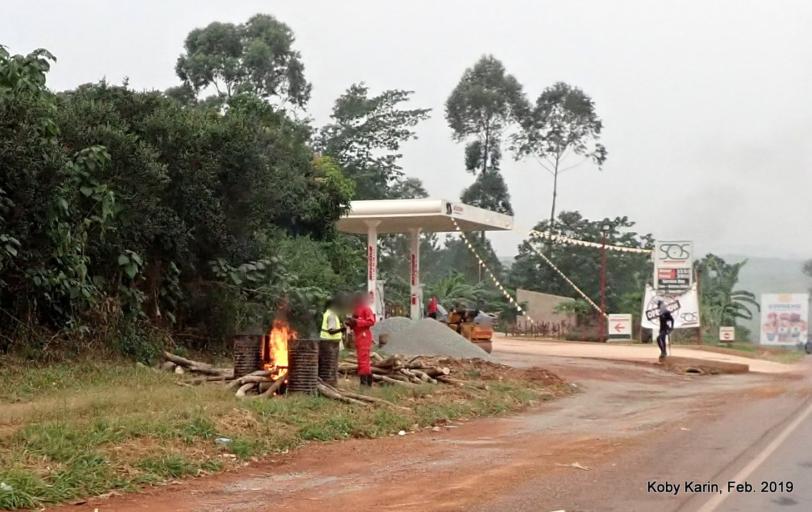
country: UG
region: Central Region
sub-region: Buikwe District
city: Njeru
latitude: 0.4163
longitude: 33.1399
